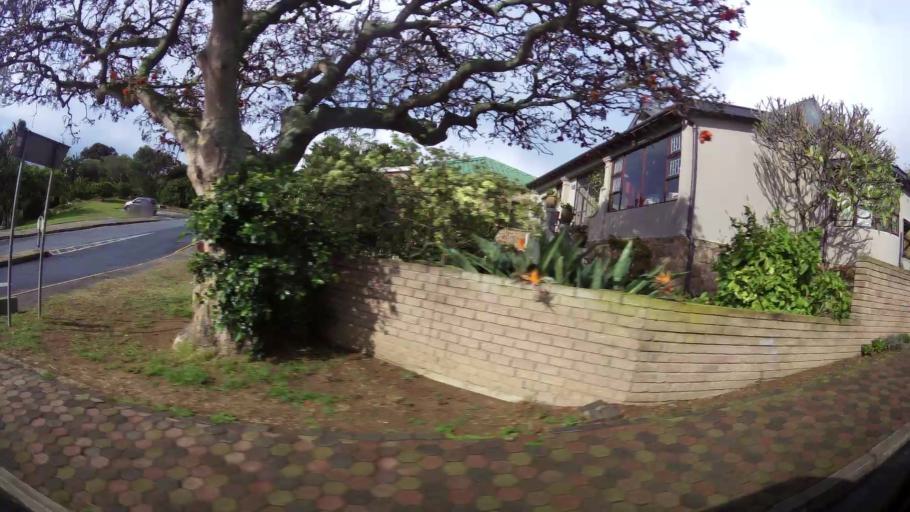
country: ZA
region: Western Cape
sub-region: Eden District Municipality
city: Mossel Bay
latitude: -34.1868
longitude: 22.1398
